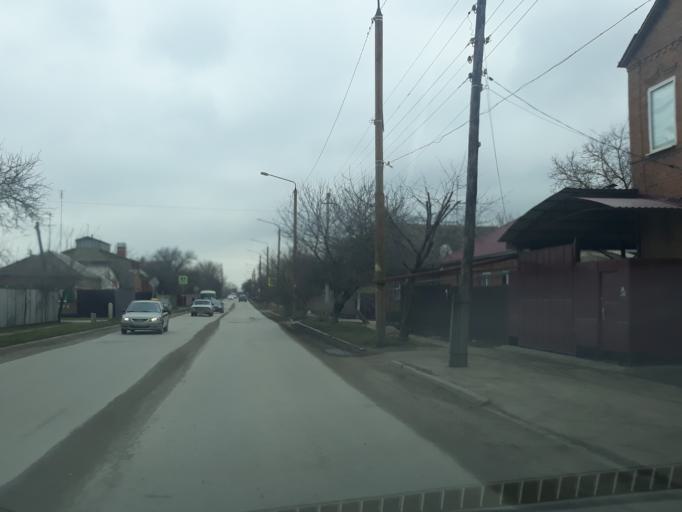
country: RU
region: Rostov
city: Taganrog
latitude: 47.2665
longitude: 38.8914
